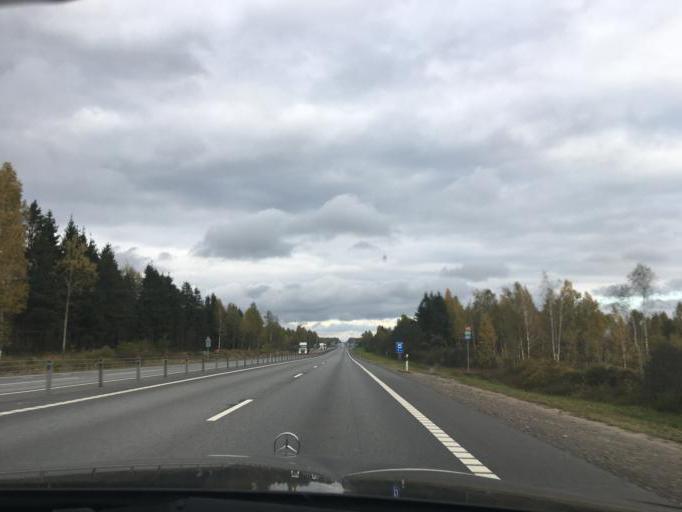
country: BY
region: Vitebsk
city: Dubrowna
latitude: 54.6898
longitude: 30.9216
